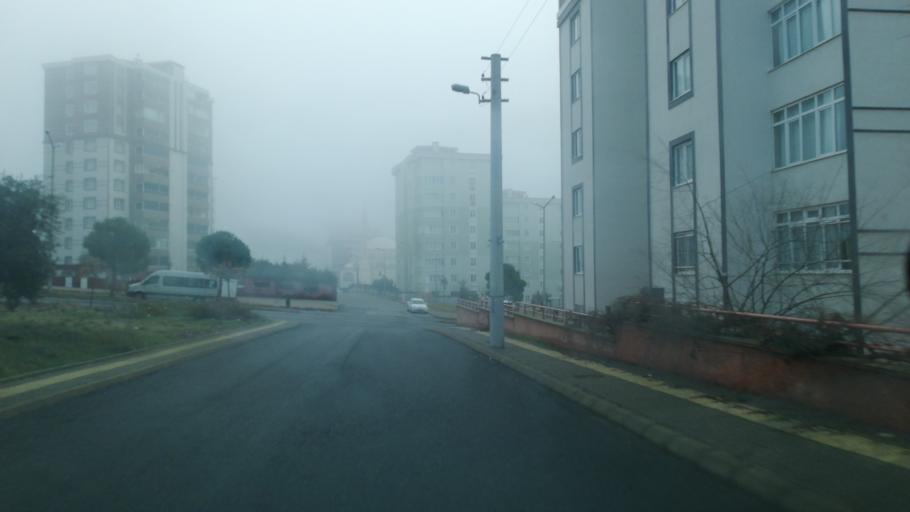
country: TR
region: Kahramanmaras
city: Kahramanmaras
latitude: 37.5975
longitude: 36.8963
